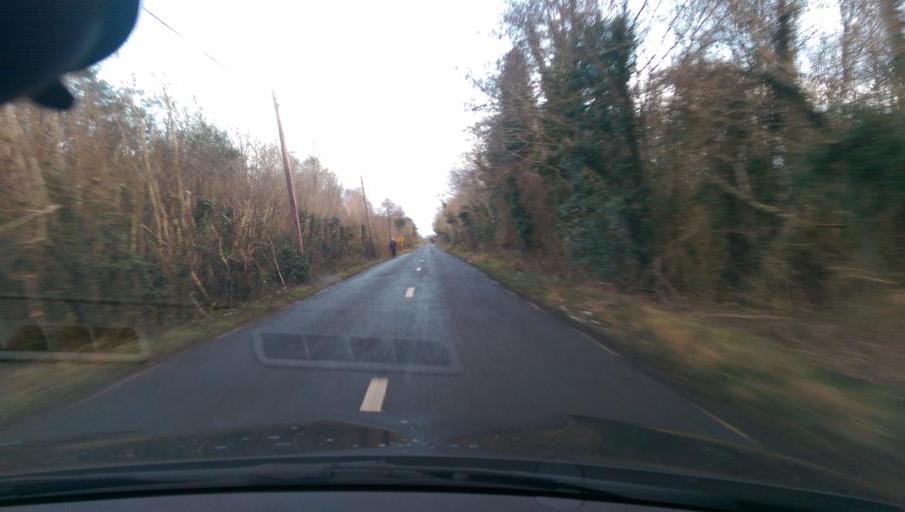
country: IE
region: Connaught
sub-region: County Galway
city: Ballinasloe
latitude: 53.3590
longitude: -8.2573
